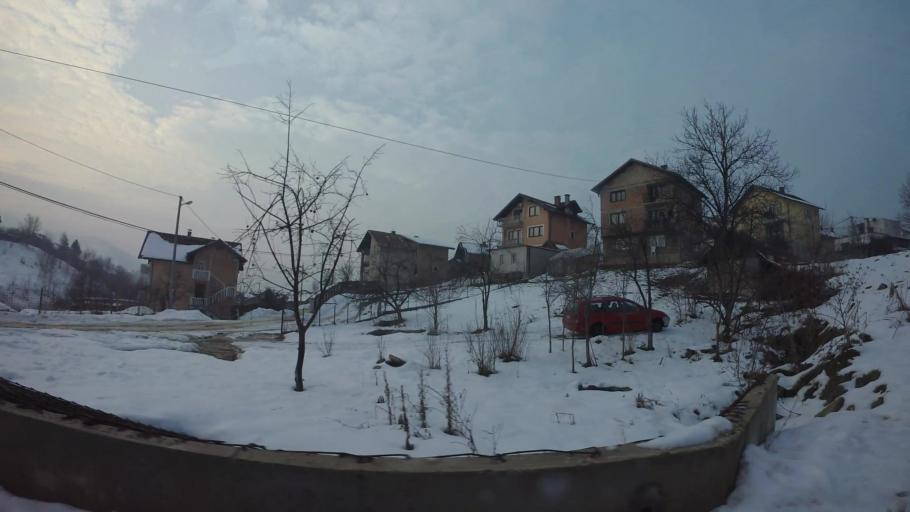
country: BA
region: Federation of Bosnia and Herzegovina
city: Hotonj
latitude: 43.8965
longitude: 18.3781
